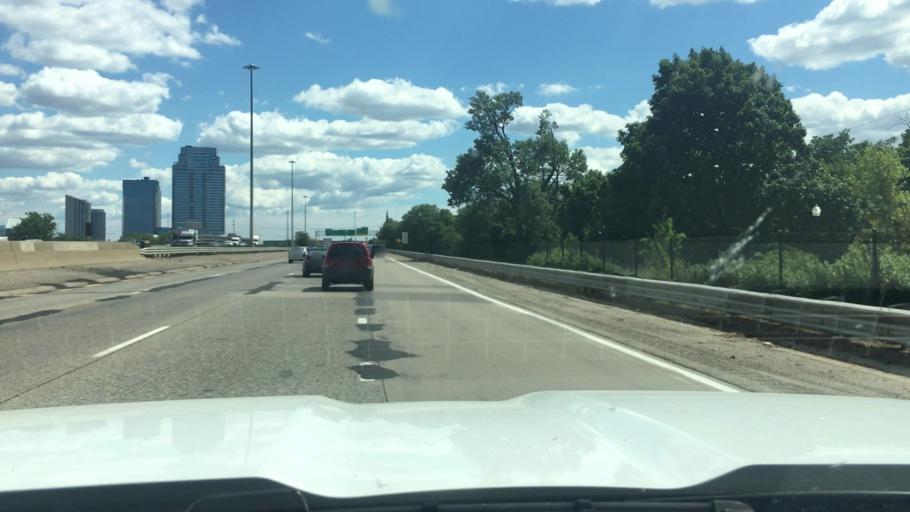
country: US
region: Michigan
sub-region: Kent County
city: Grand Rapids
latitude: 42.9802
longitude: -85.6776
